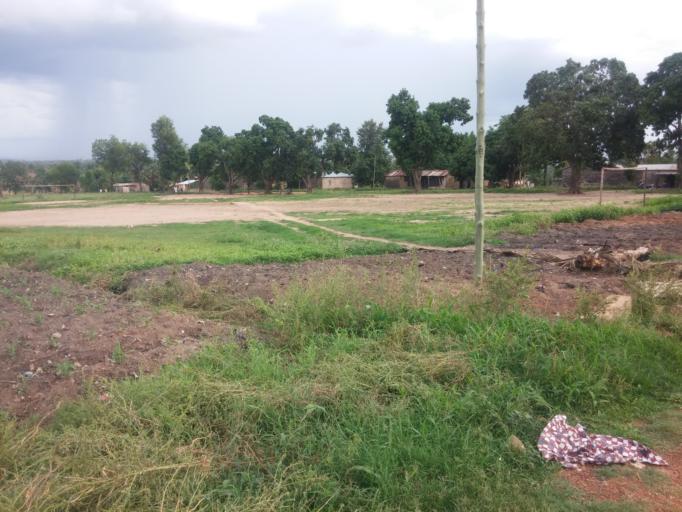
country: TG
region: Kara
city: Kara
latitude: 9.5466
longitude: 1.2059
